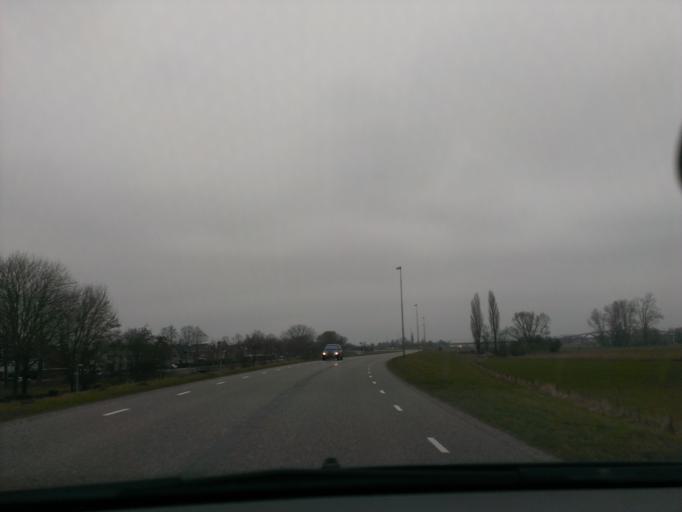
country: NL
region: Gelderland
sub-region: Gemeente Hattem
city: Hattem
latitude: 52.4785
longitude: 6.0650
